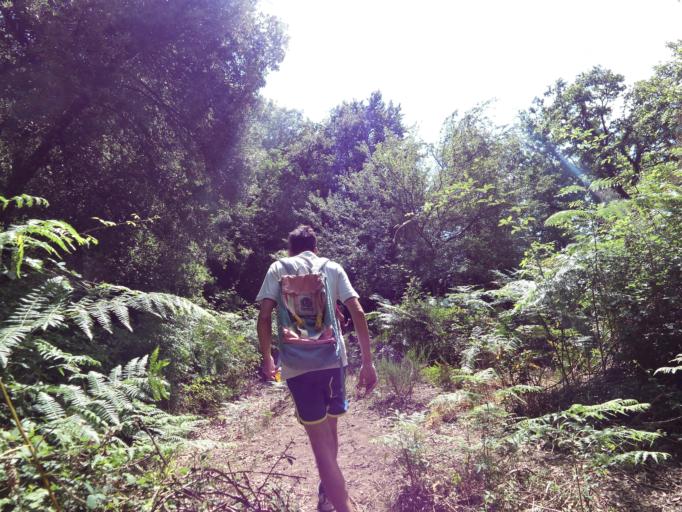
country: IT
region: Calabria
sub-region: Provincia di Vibo-Valentia
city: Nardodipace
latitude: 38.5078
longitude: 16.3866
